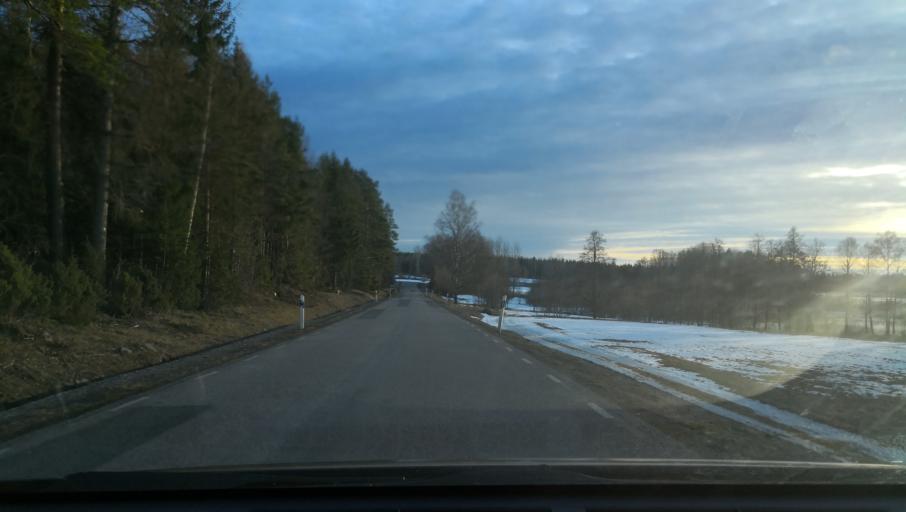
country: SE
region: Uppsala
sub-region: Osthammars Kommun
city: Osterbybruk
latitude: 60.2474
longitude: 17.9373
